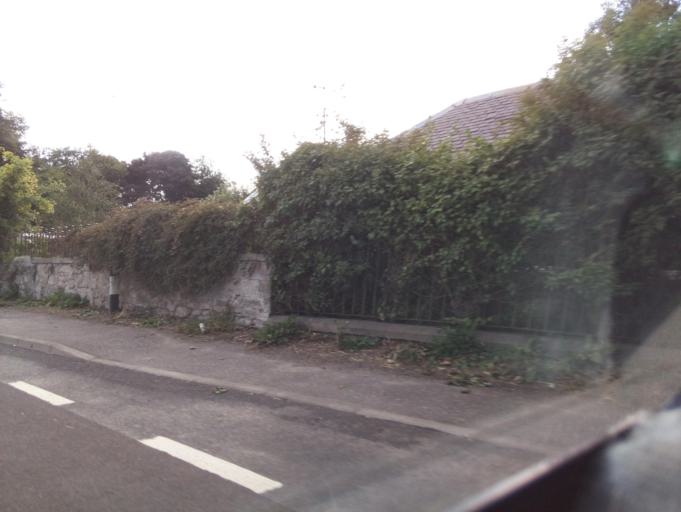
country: GB
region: Scotland
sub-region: Midlothian
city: Penicuik
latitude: 55.8675
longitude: -3.2126
